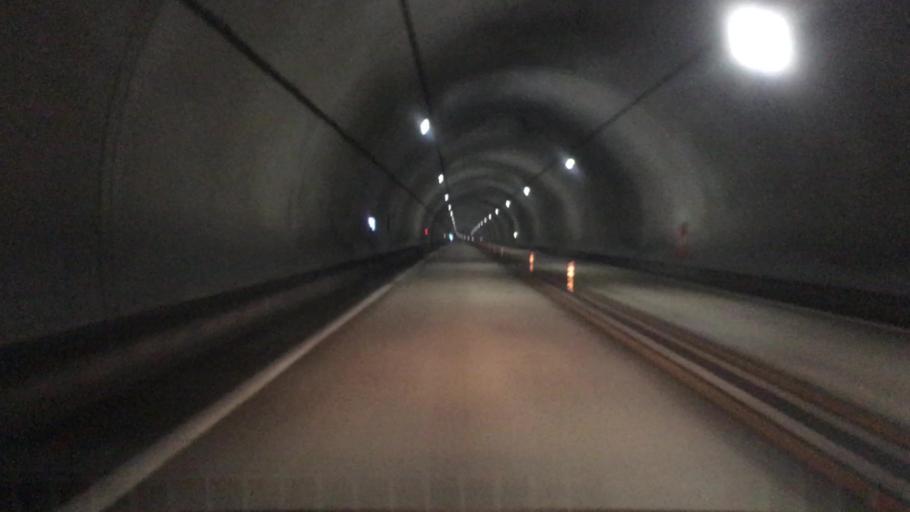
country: JP
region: Tottori
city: Tottori
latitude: 35.6066
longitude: 134.3817
